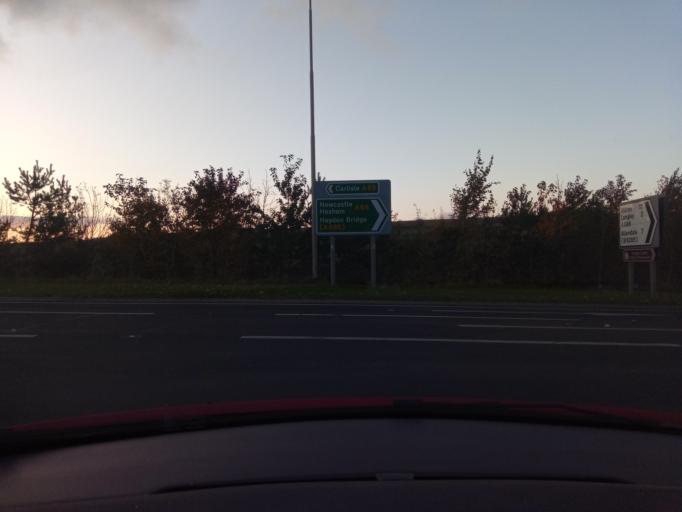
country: GB
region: England
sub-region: Northumberland
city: Warden
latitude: 54.9730
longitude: -2.2362
